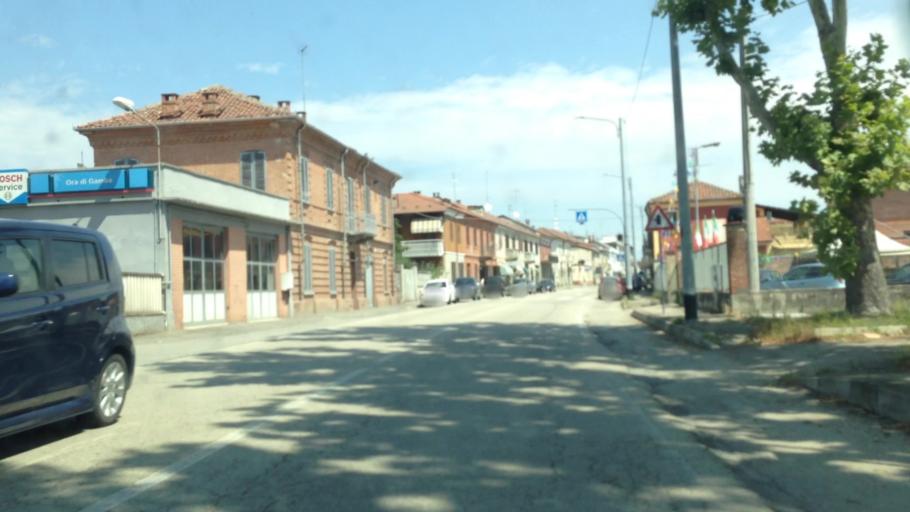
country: IT
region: Piedmont
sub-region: Provincia di Asti
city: Castell'Alfero
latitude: 44.9553
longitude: 8.2230
